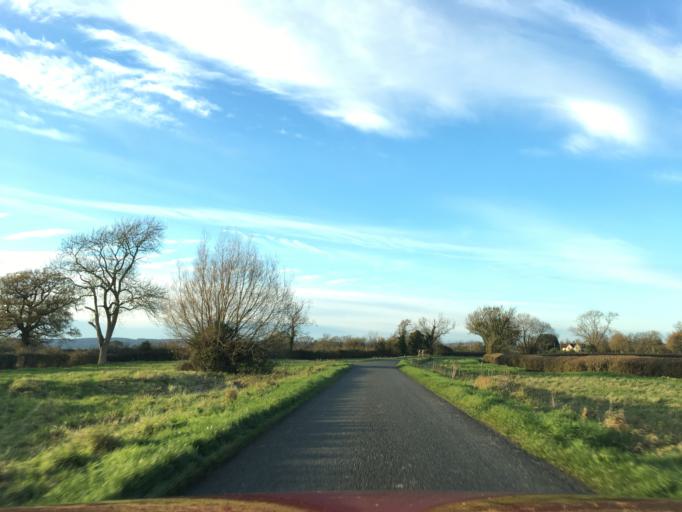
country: GB
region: England
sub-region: South Gloucestershire
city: Hill
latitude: 51.6496
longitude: -2.5167
